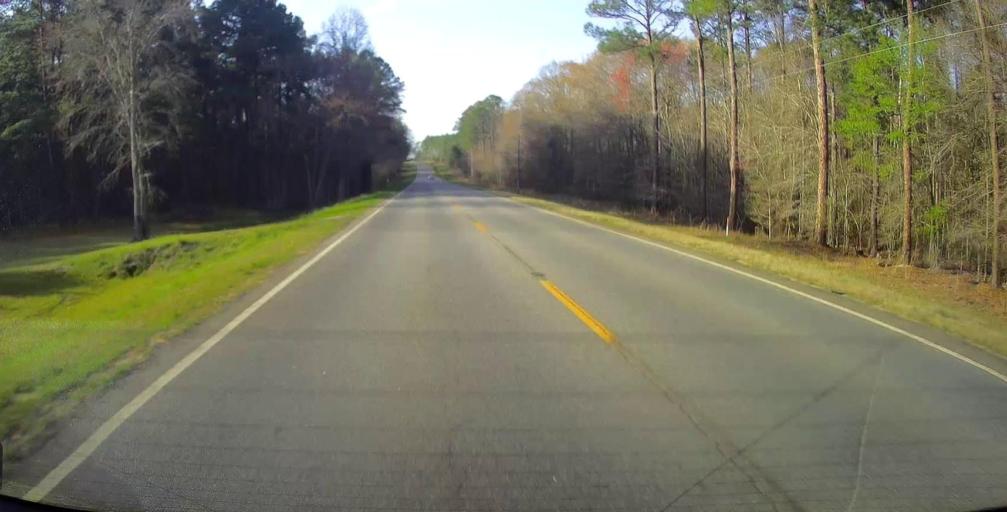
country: US
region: Georgia
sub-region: Toombs County
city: Lyons
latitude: 32.1666
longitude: -82.2727
